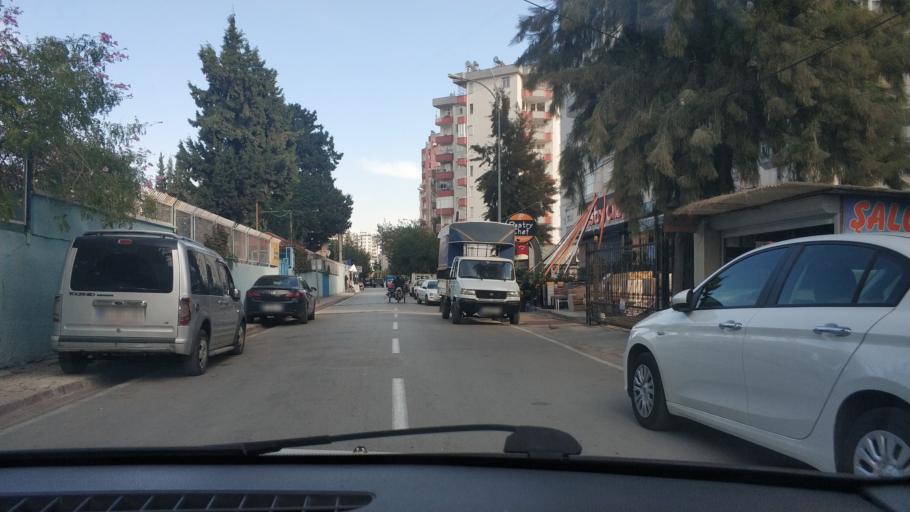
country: TR
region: Adana
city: Adana
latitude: 37.0064
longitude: 35.3175
